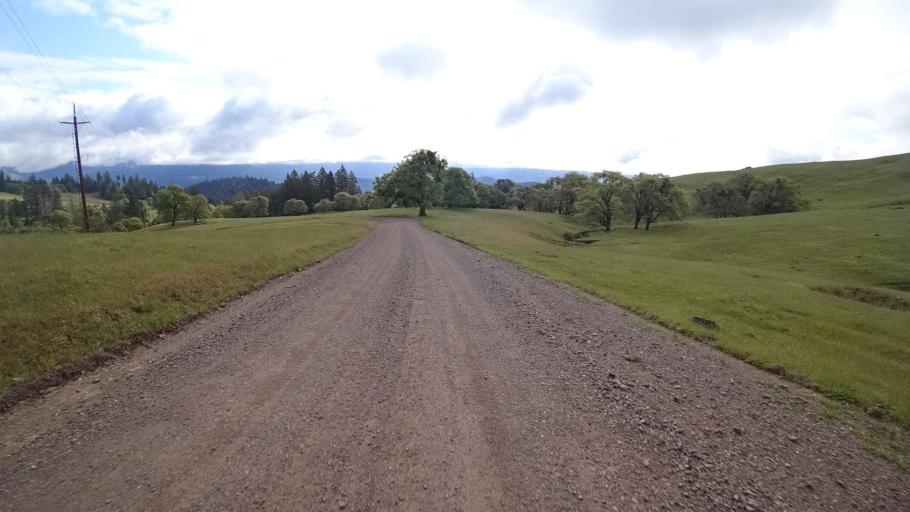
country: US
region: California
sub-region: Humboldt County
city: Redway
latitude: 40.2046
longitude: -123.6919
